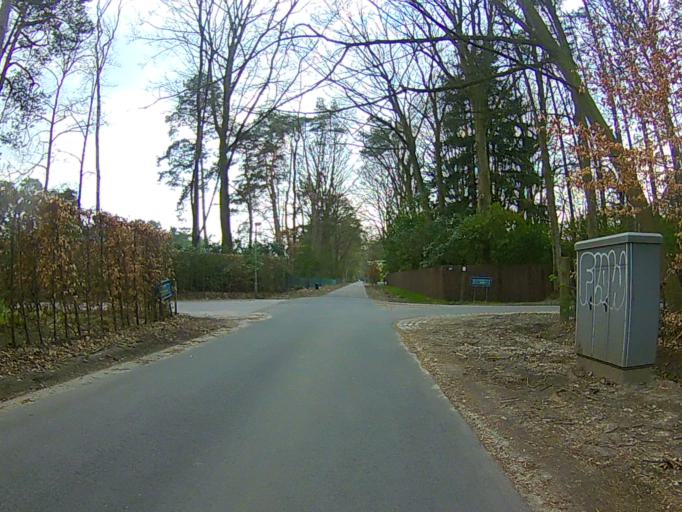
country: BE
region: Flanders
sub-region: Provincie Antwerpen
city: Kapellen
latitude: 51.3456
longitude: 4.4601
